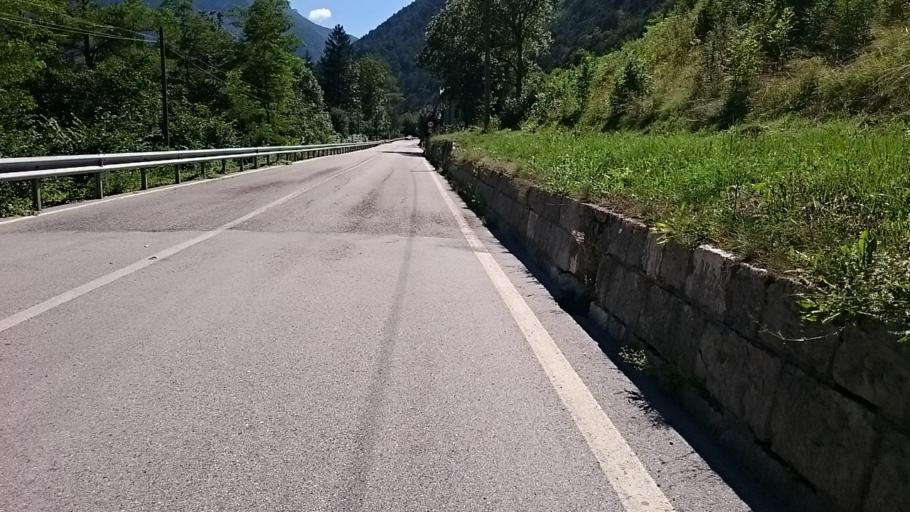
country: IT
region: Veneto
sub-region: Provincia di Belluno
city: Perarolo di Cadore
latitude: 46.3865
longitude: 12.3533
